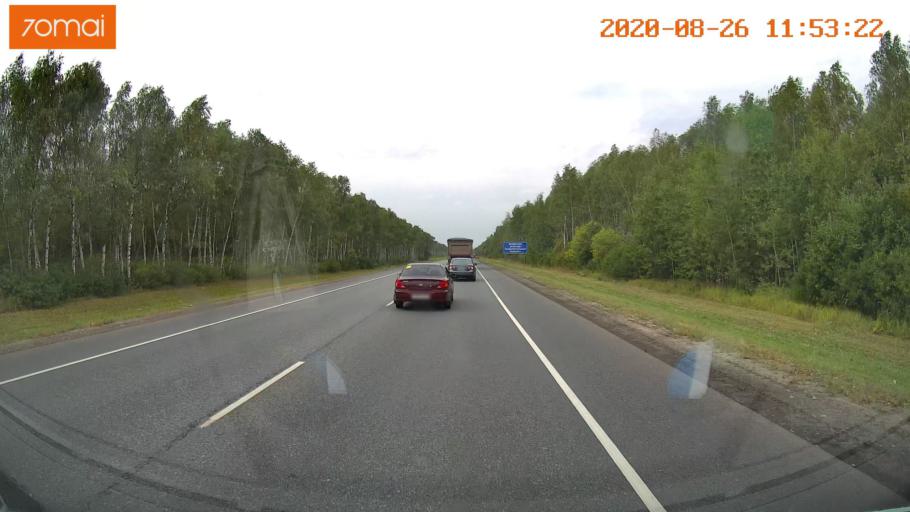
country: RU
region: Rjazan
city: Kiritsy
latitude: 54.2913
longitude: 40.4330
